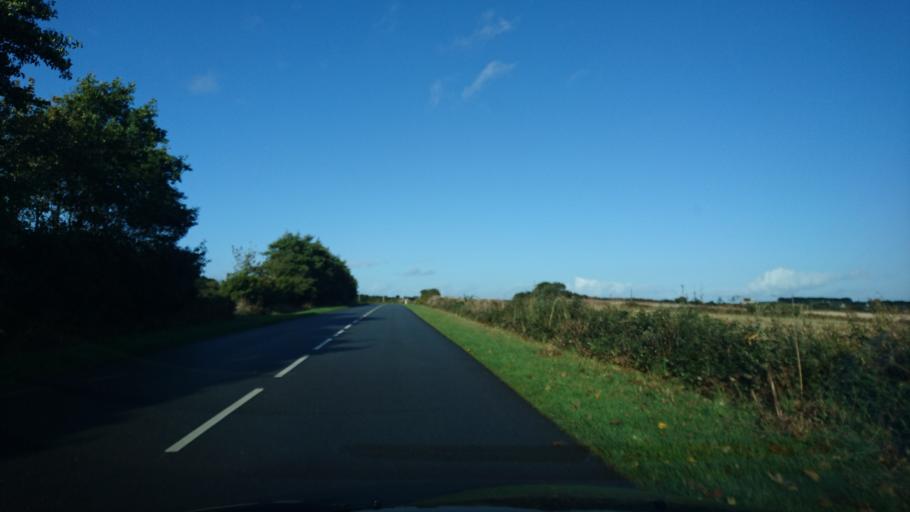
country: FR
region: Brittany
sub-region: Departement du Finistere
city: Plouarzel
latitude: 48.4395
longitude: -4.7350
